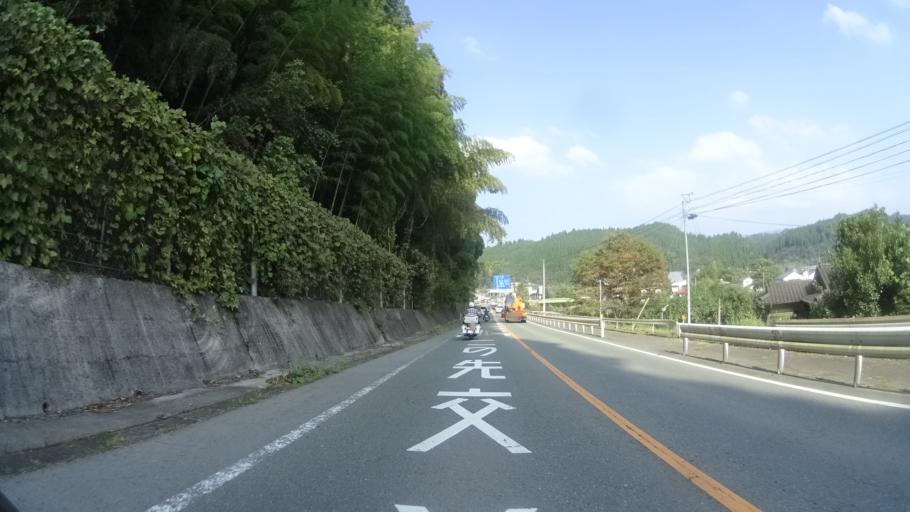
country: JP
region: Kumamoto
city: Aso
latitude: 33.0957
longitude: 131.0666
